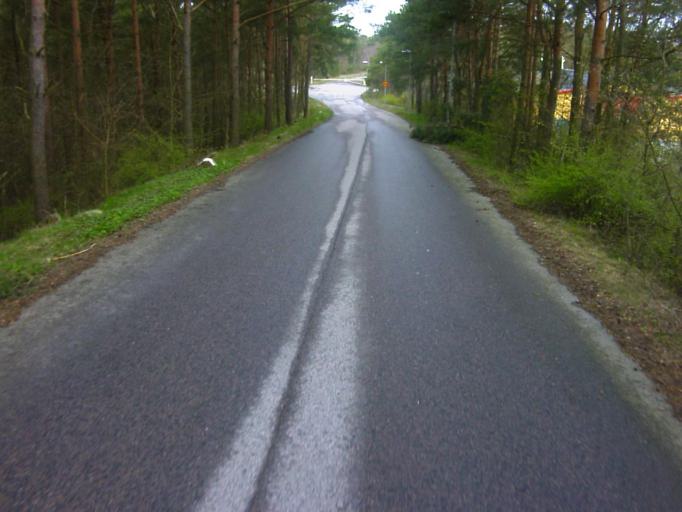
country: SE
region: Skane
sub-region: Kavlinge Kommun
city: Kaevlinge
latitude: 55.7705
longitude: 13.0781
